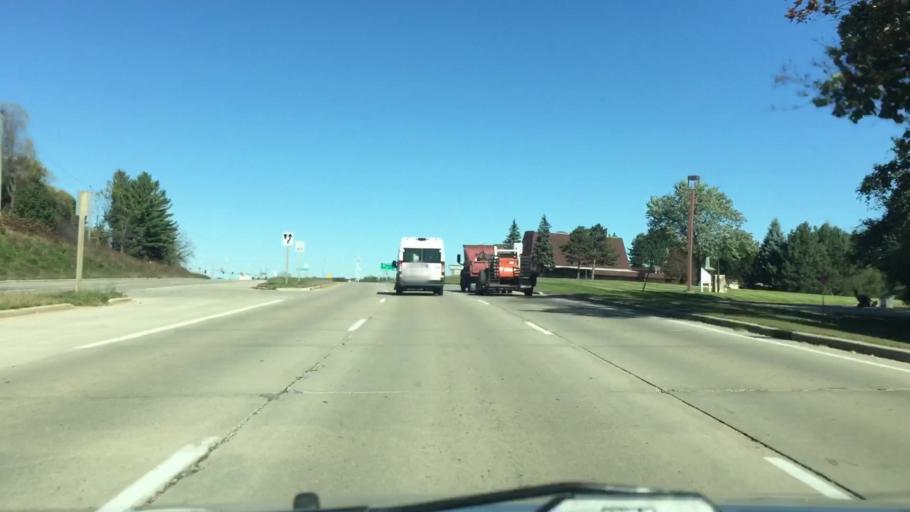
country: US
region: Wisconsin
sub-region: Waukesha County
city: Waukesha
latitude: 42.9996
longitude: -88.1994
